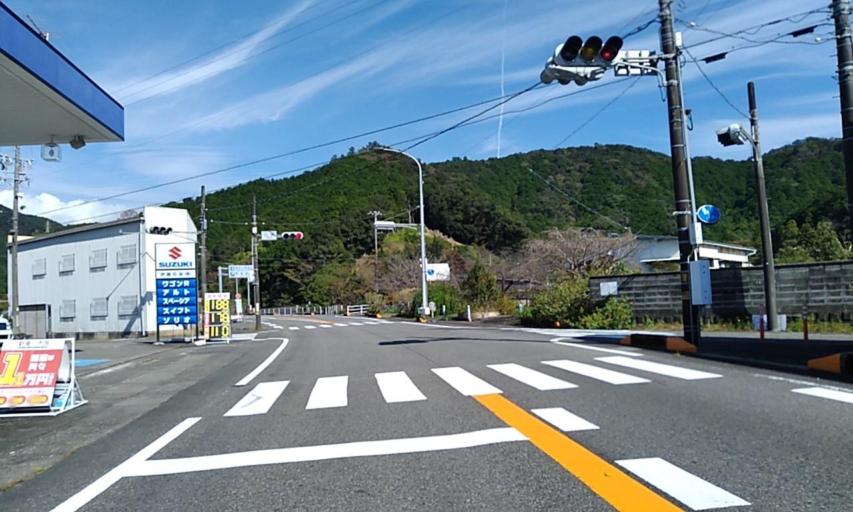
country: JP
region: Mie
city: Owase
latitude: 34.1638
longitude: 136.2811
